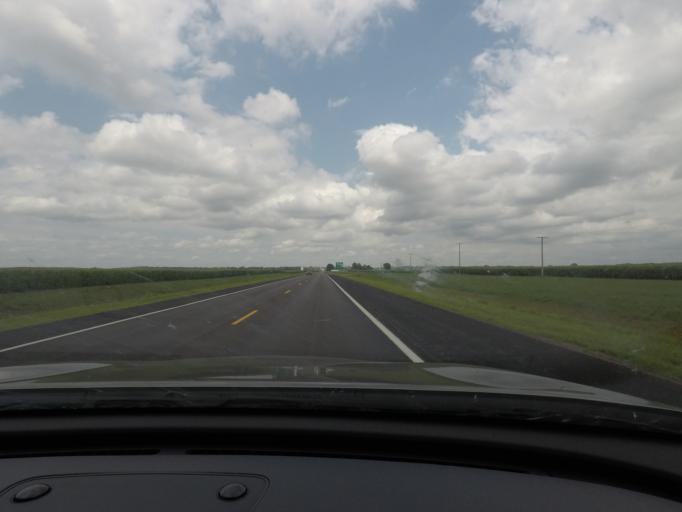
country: US
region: Missouri
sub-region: Carroll County
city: Carrollton
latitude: 39.3252
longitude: -93.4957
